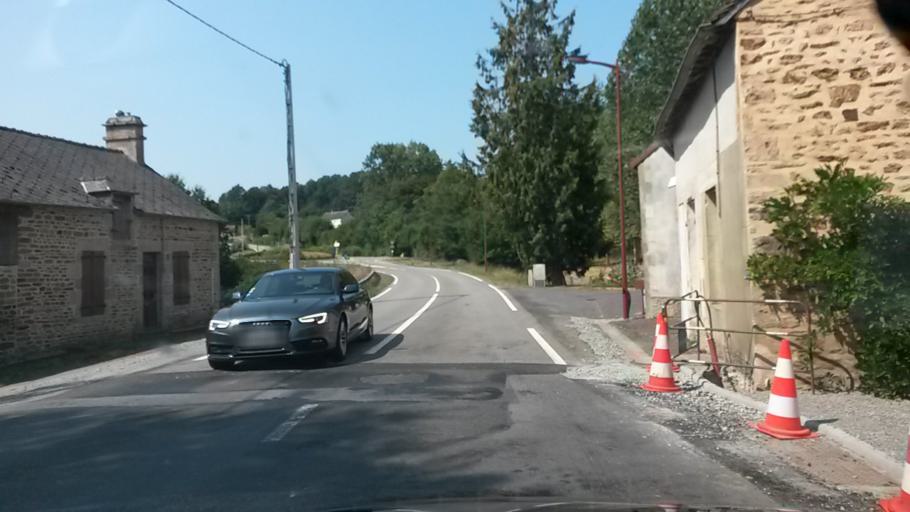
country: FR
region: Lower Normandy
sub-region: Departement de l'Orne
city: Saint-Denis-sur-Sarthon
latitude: 48.4145
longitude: -0.0356
